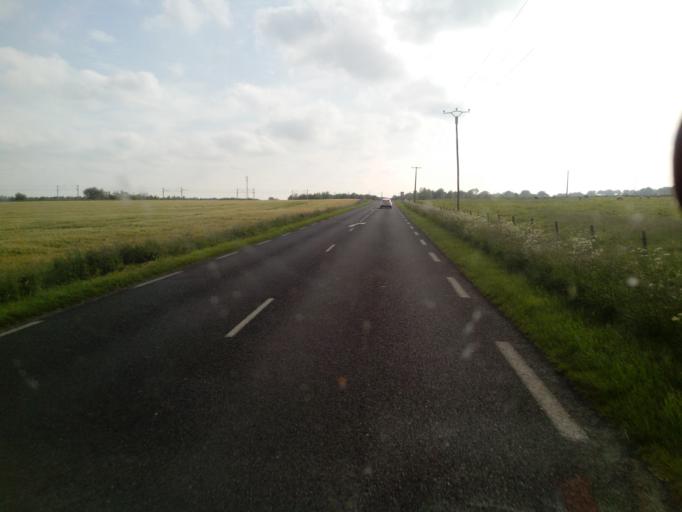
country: FR
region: Haute-Normandie
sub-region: Departement de la Seine-Maritime
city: Sainte-Marie-des-Champs
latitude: 49.6354
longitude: 0.8177
